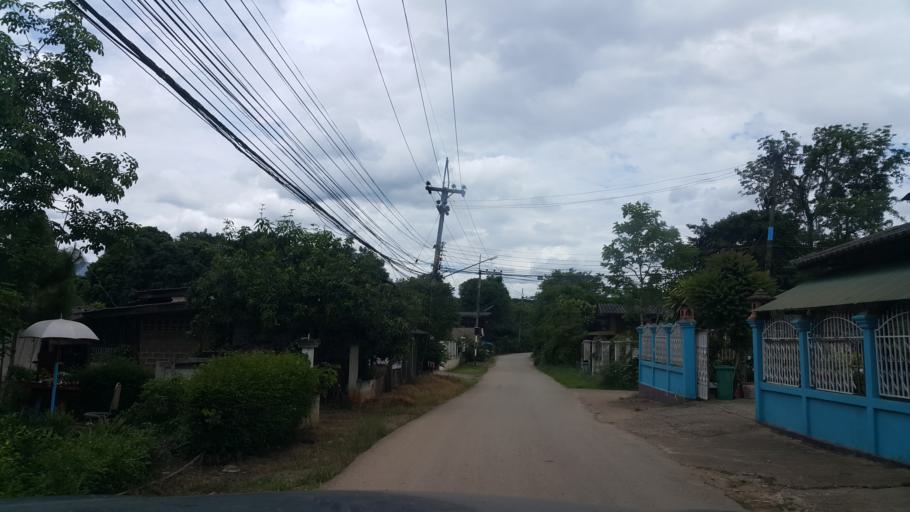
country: TH
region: Chiang Mai
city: Mae Taeng
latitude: 19.1928
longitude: 98.9822
